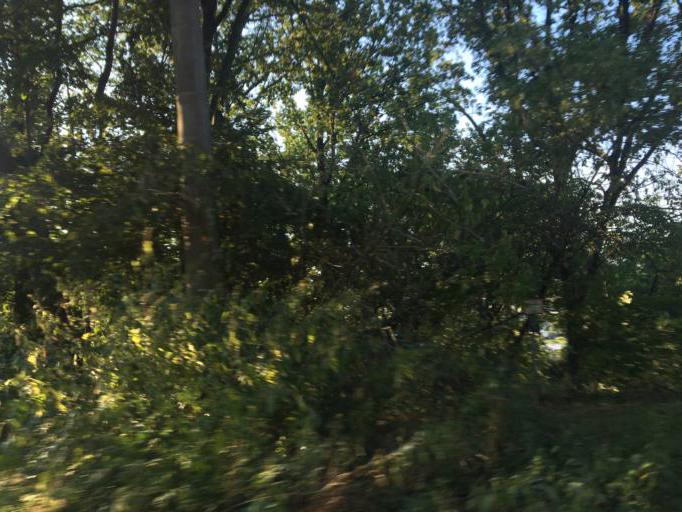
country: DE
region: Saxony
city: Coswig
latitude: 51.0884
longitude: 13.6034
